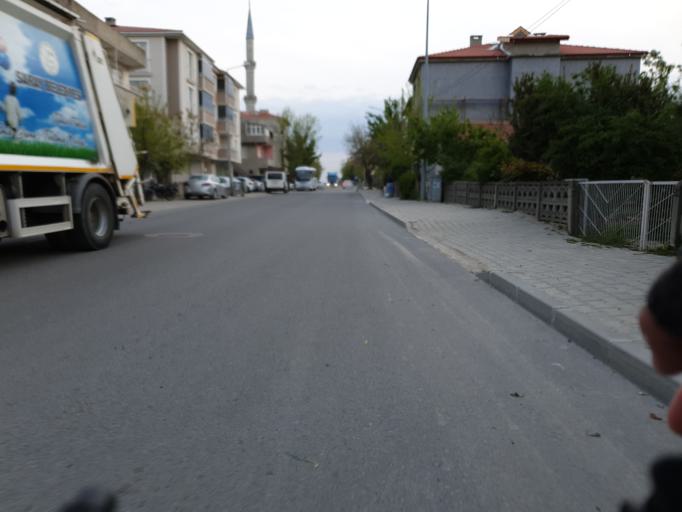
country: TR
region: Tekirdag
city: Saray
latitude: 41.4368
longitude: 27.9159
